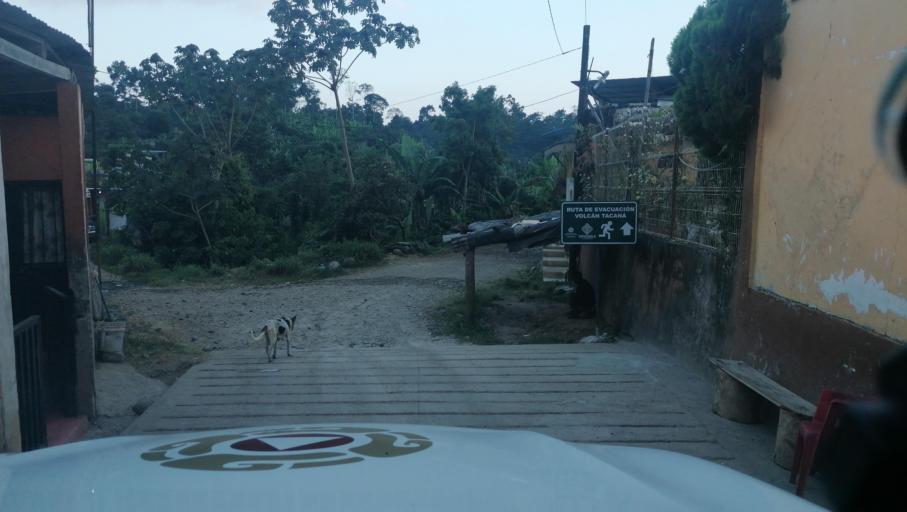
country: MX
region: Chiapas
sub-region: Cacahoatan
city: Benito Juarez
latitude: 15.0793
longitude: -92.2236
